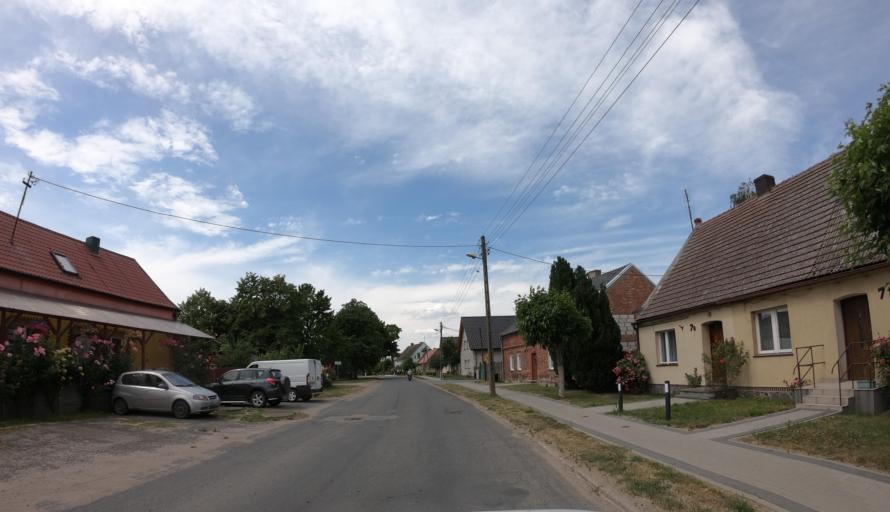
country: PL
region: West Pomeranian Voivodeship
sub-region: Powiat pyrzycki
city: Kozielice
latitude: 53.1053
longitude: 14.8283
